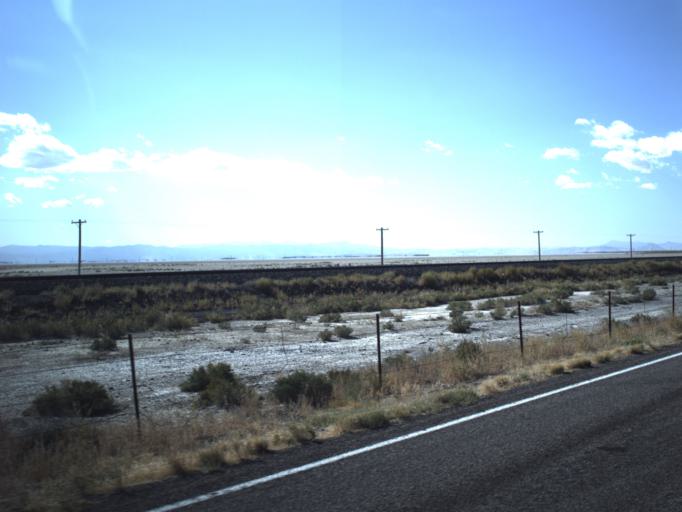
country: US
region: Utah
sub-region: Millard County
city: Delta
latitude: 39.1852
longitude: -112.6973
